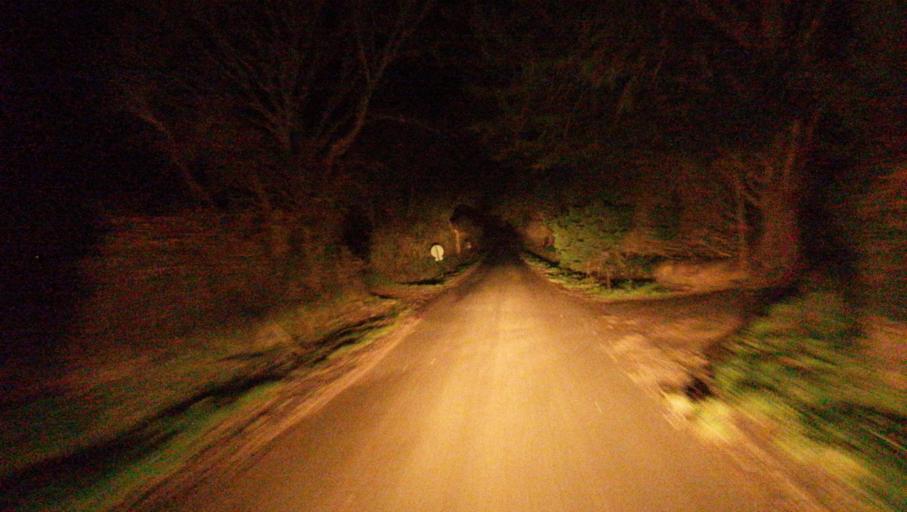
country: FR
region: Brittany
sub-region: Departement des Cotes-d'Armor
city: Lanvollon
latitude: 48.6501
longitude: -3.0206
